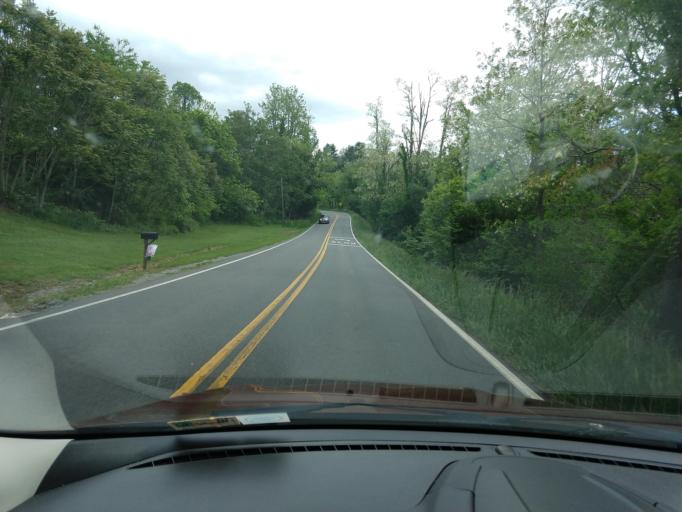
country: US
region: Virginia
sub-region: Wythe County
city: Wytheville
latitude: 36.8963
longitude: -80.9700
